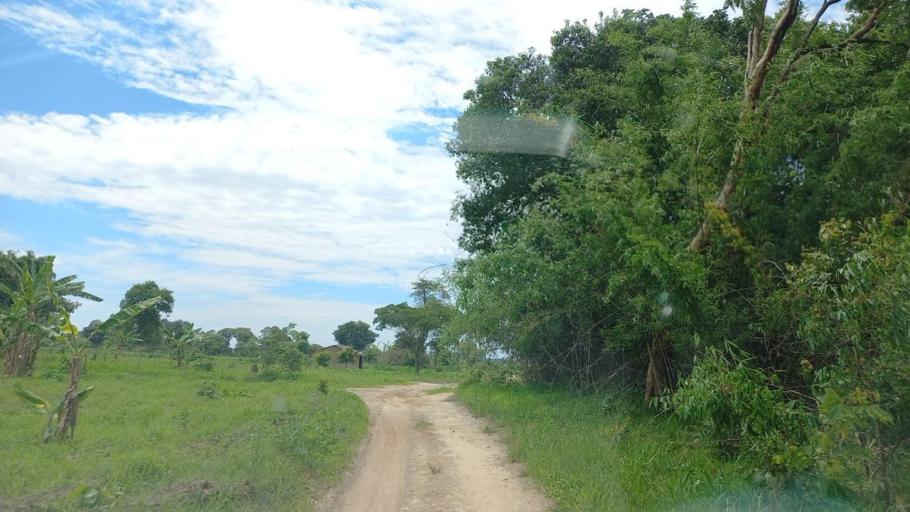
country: ZM
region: Copperbelt
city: Kitwe
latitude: -12.8015
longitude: 28.4013
